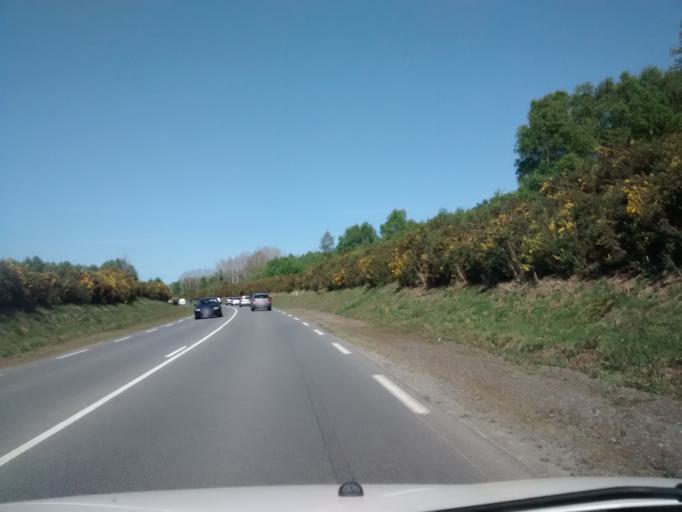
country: FR
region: Brittany
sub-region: Departement d'Ille-et-Vilaine
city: Pleurtuit
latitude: 48.5850
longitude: -2.0700
